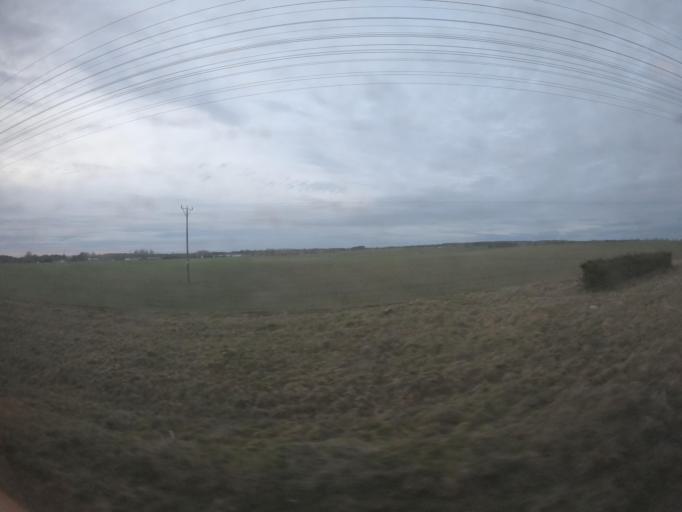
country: PL
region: West Pomeranian Voivodeship
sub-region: Powiat drawski
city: Czaplinek
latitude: 53.5462
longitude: 16.2742
